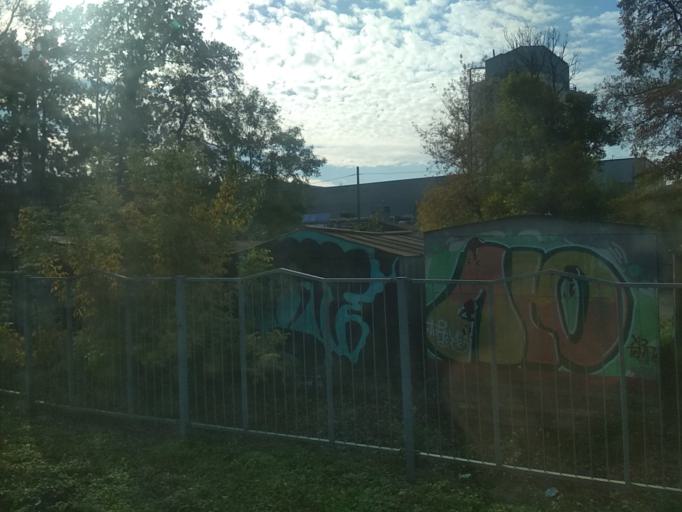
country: BY
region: Minsk
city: Syenitsa
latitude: 53.8435
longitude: 27.5572
